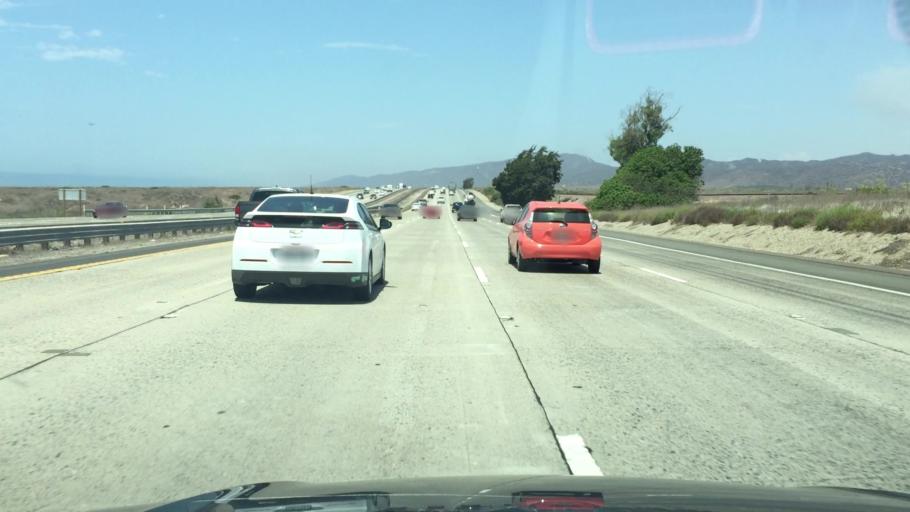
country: US
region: California
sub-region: San Diego County
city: Camp Pendleton South
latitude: 33.2784
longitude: -117.4467
